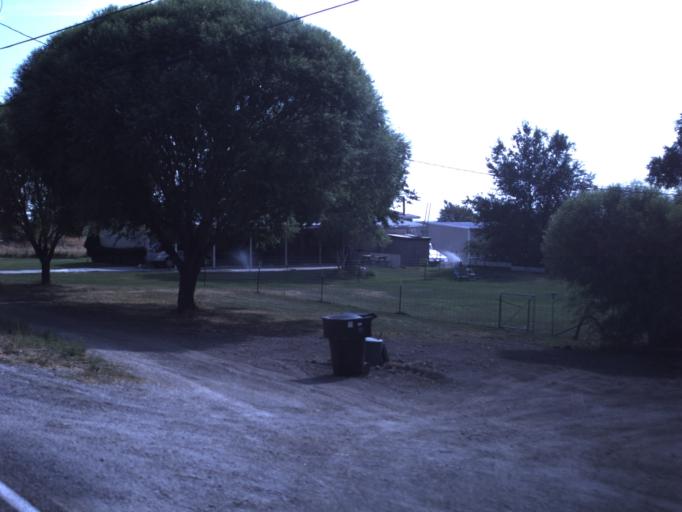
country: US
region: Utah
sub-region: Box Elder County
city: Honeyville
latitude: 41.5937
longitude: -112.0456
